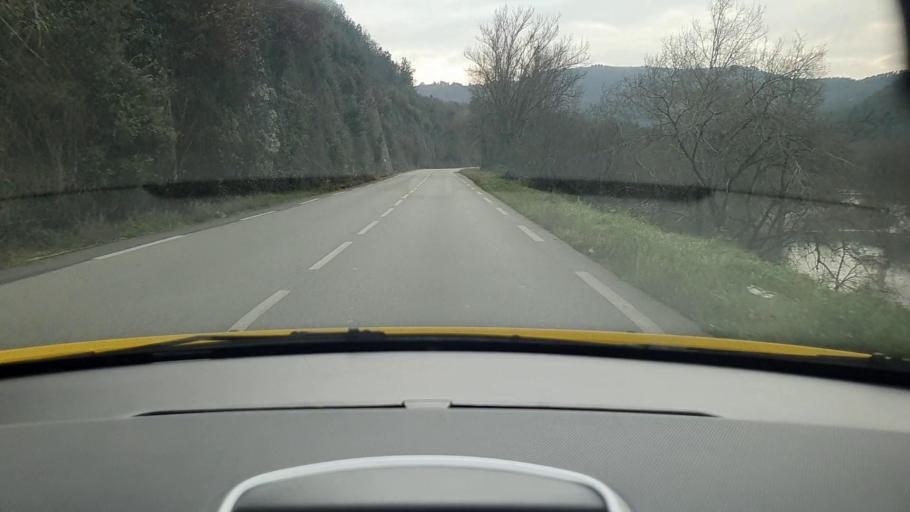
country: FR
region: Languedoc-Roussillon
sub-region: Departement du Gard
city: Molieres-sur-Ceze
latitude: 44.2728
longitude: 4.1529
